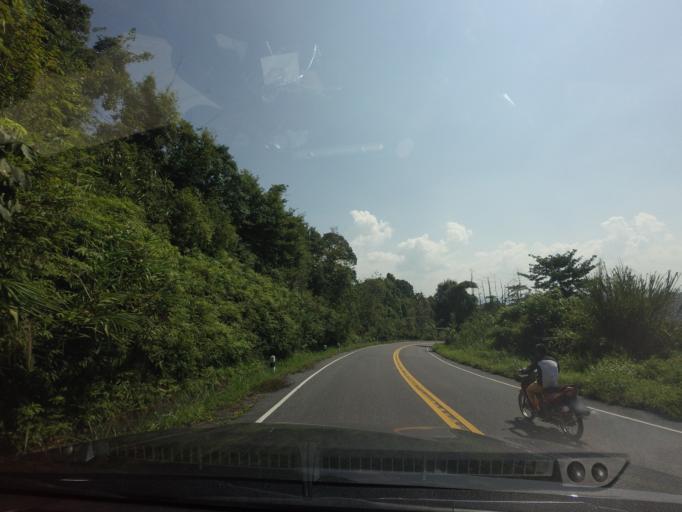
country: TH
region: Nan
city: Bo Kluea
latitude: 19.0345
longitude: 101.0844
